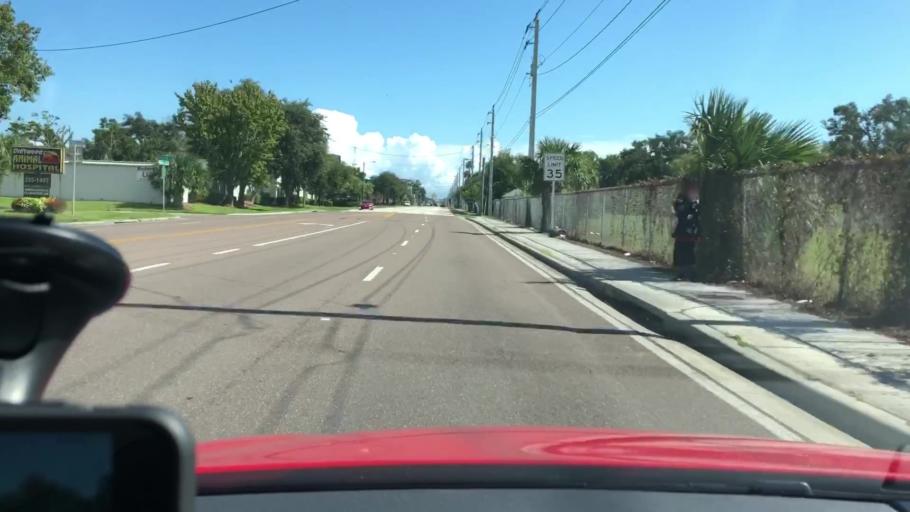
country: US
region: Florida
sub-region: Volusia County
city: Holly Hill
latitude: 29.2202
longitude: -81.0462
